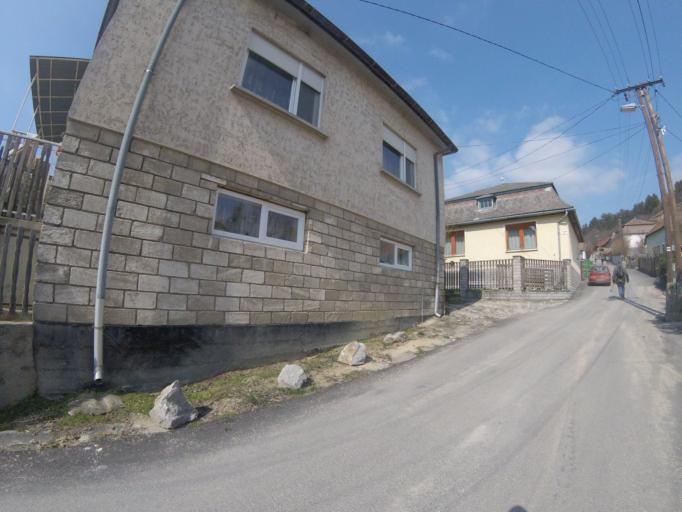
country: HU
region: Komarom-Esztergom
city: Nyergesujfalu
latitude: 47.7298
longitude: 18.5579
